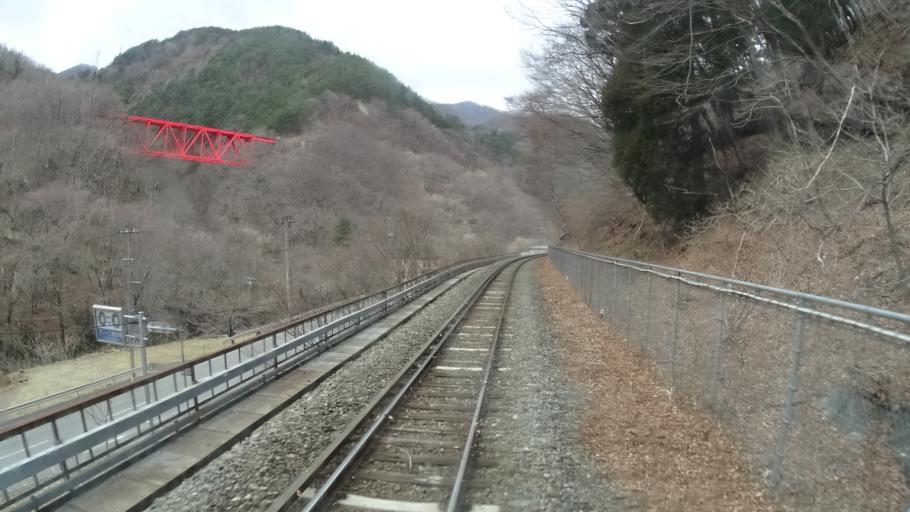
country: JP
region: Iwate
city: Kamaishi
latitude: 39.2761
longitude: 141.7218
